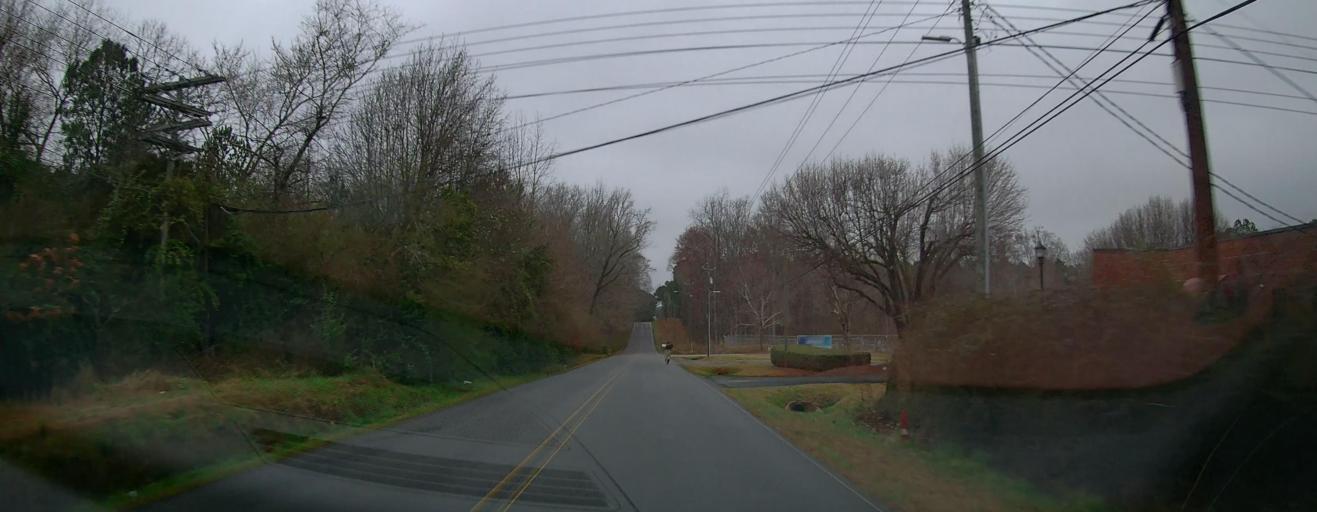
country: US
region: Georgia
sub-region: Pike County
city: Zebulon
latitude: 33.1147
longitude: -84.3432
